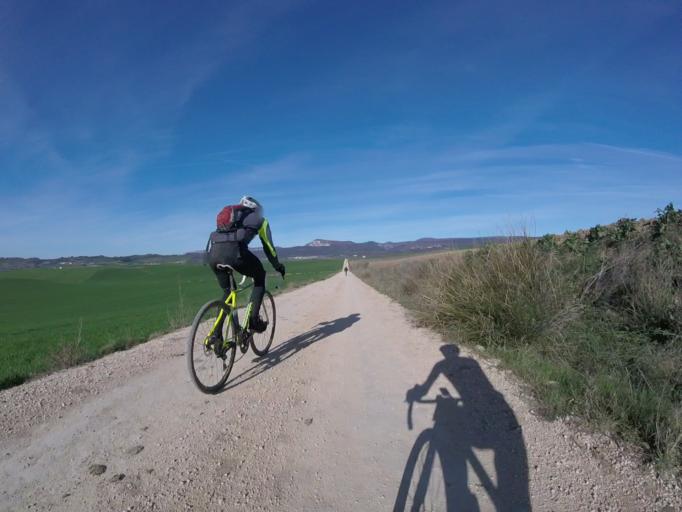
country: ES
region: Navarre
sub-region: Provincia de Navarra
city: Yerri
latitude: 42.7133
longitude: -1.9720
